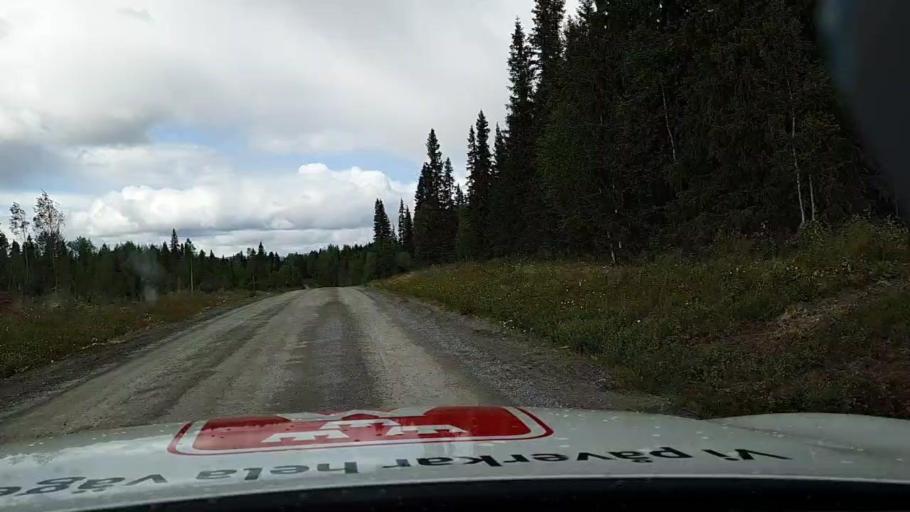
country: SE
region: Jaemtland
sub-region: Krokoms Kommun
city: Valla
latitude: 63.6597
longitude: 13.7592
